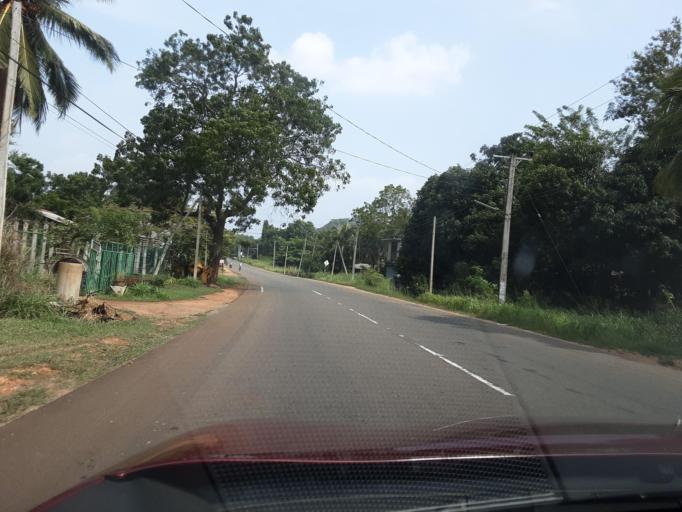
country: LK
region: North Central
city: Anuradhapura
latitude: 8.3401
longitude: 80.5035
